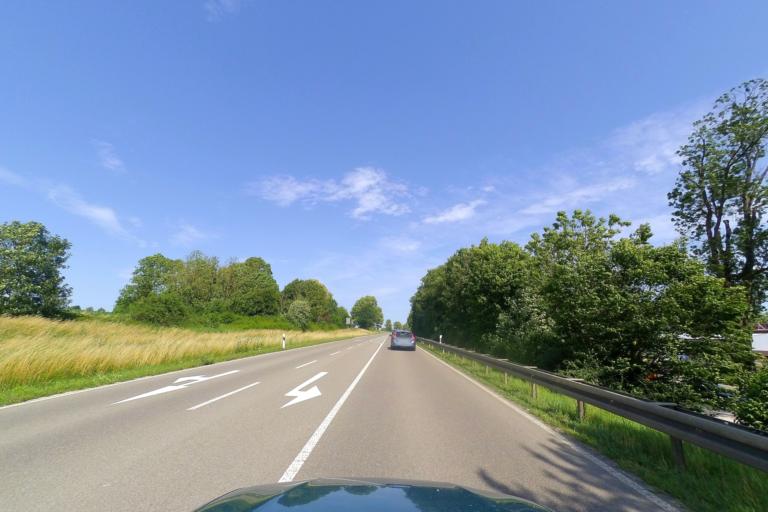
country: DE
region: Baden-Wuerttemberg
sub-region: Regierungsbezirk Stuttgart
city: Nattheim
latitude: 48.6929
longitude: 10.2293
